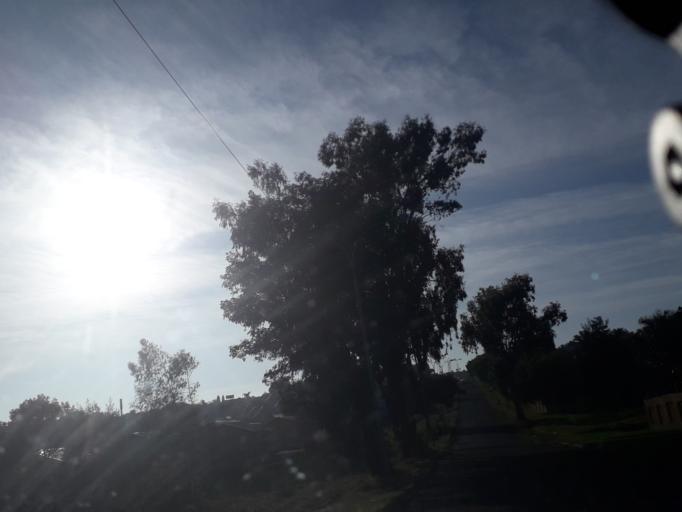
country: ZA
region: Gauteng
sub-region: City of Johannesburg Metropolitan Municipality
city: Roodepoort
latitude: -26.1021
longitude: 27.9199
